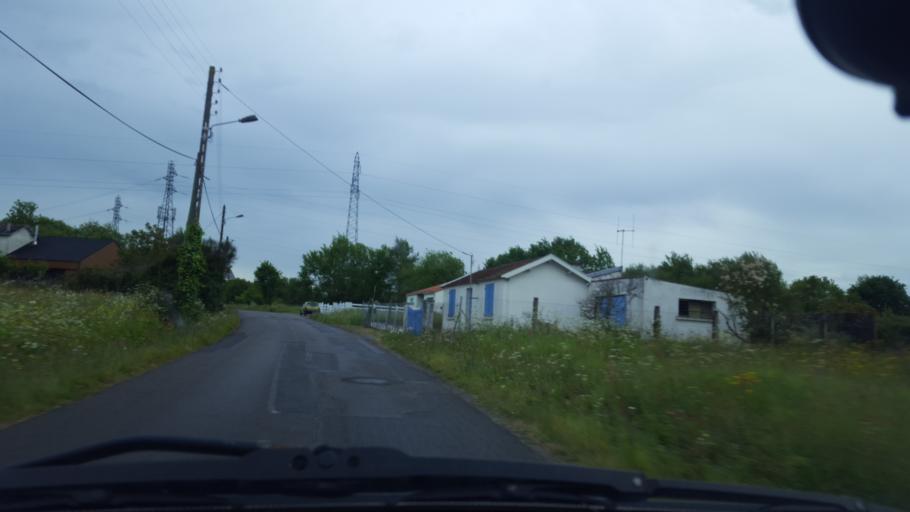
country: FR
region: Pays de la Loire
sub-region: Departement de la Loire-Atlantique
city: Les Sorinieres
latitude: 47.1682
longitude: -1.5264
